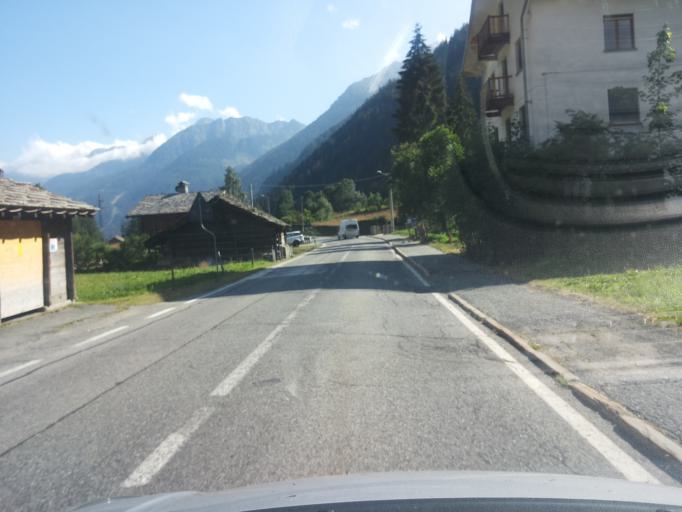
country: IT
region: Aosta Valley
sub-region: Valle d'Aosta
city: Gressoney-Saint-Jean
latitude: 45.7986
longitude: 7.8226
